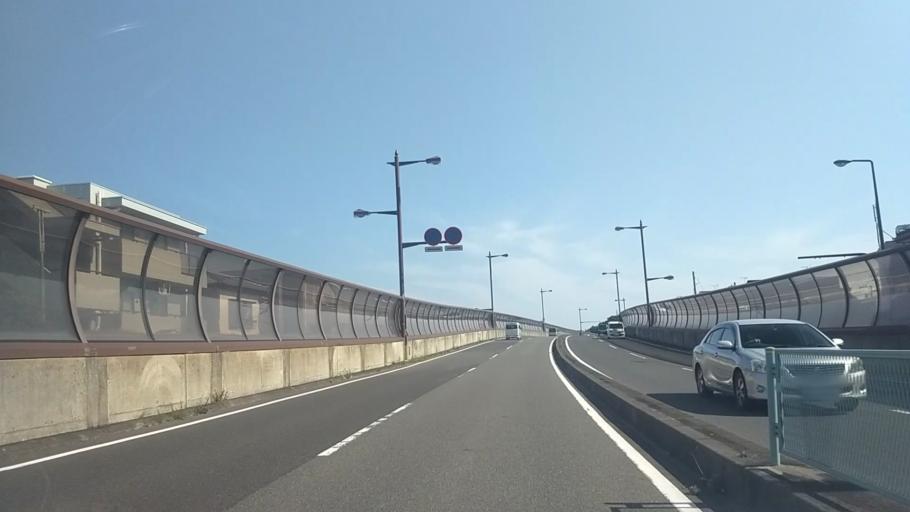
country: JP
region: Kanagawa
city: Fujisawa
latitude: 35.3416
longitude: 139.5023
